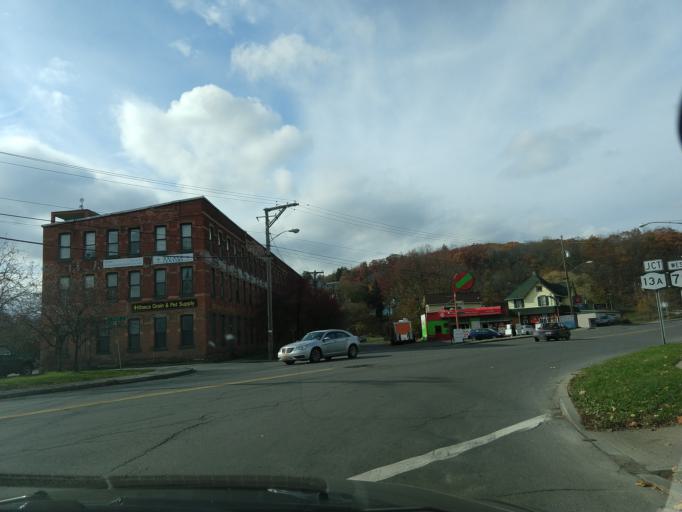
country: US
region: New York
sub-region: Tompkins County
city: Ithaca
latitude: 42.4400
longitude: -76.5130
